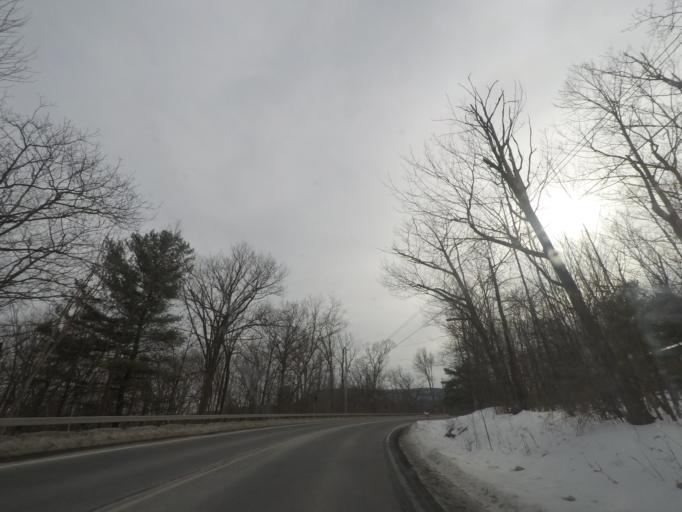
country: US
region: New York
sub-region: Albany County
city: Altamont
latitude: 42.7017
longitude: -74.0386
